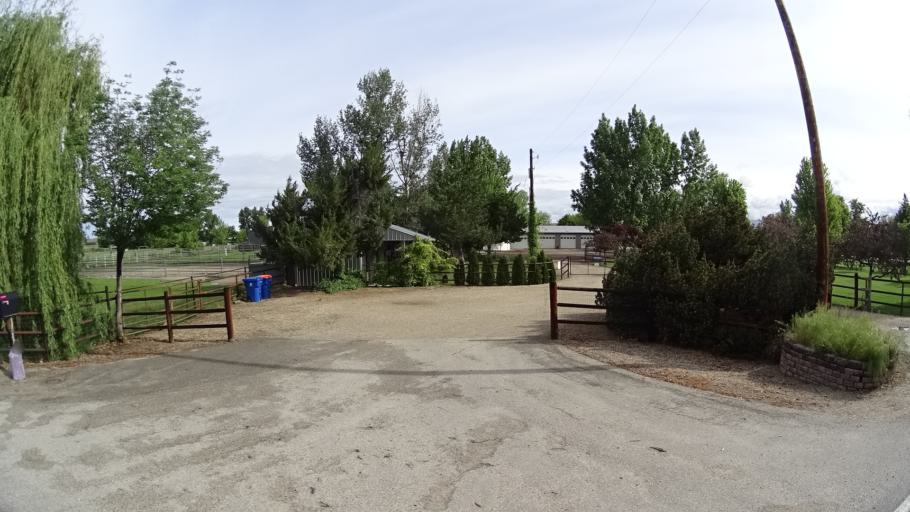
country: US
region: Idaho
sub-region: Ada County
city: Eagle
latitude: 43.7209
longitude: -116.4098
